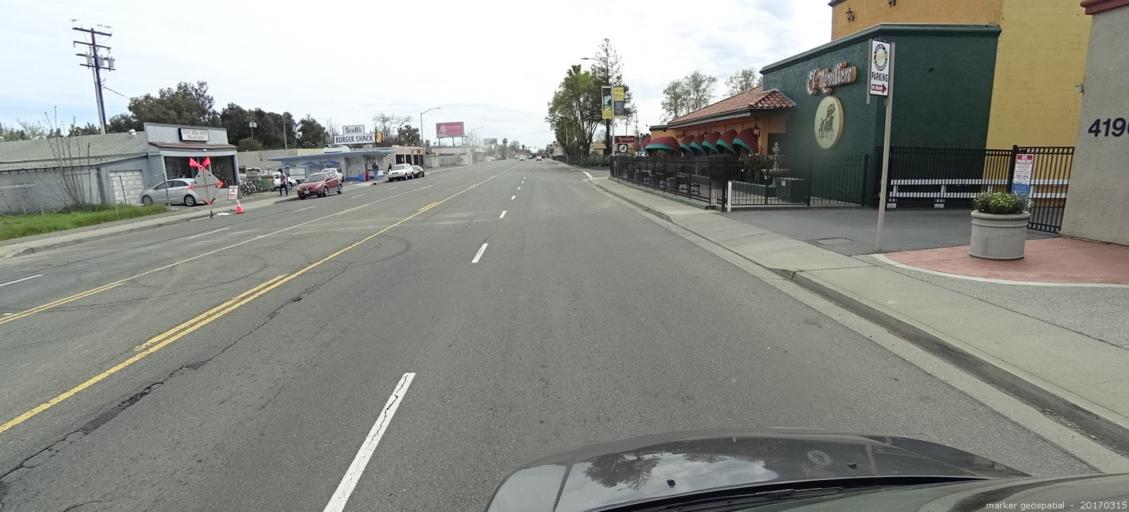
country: US
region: California
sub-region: Sacramento County
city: Parkway
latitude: 38.5369
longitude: -121.4748
